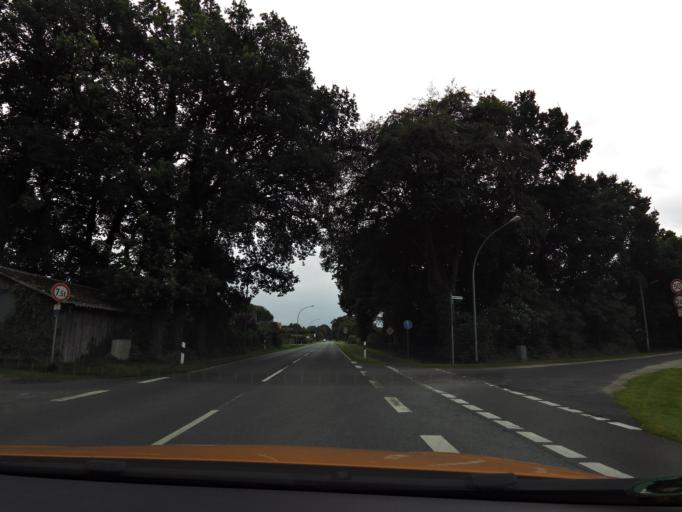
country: DE
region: Lower Saxony
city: Gross Ippener
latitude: 53.0050
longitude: 8.6105
